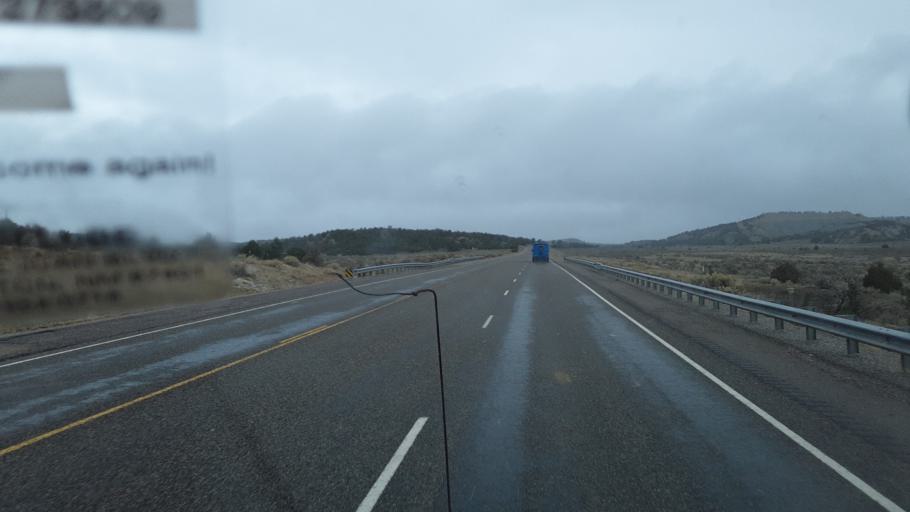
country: US
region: New Mexico
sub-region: Rio Arriba County
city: Tierra Amarilla
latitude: 36.4437
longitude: -106.4747
